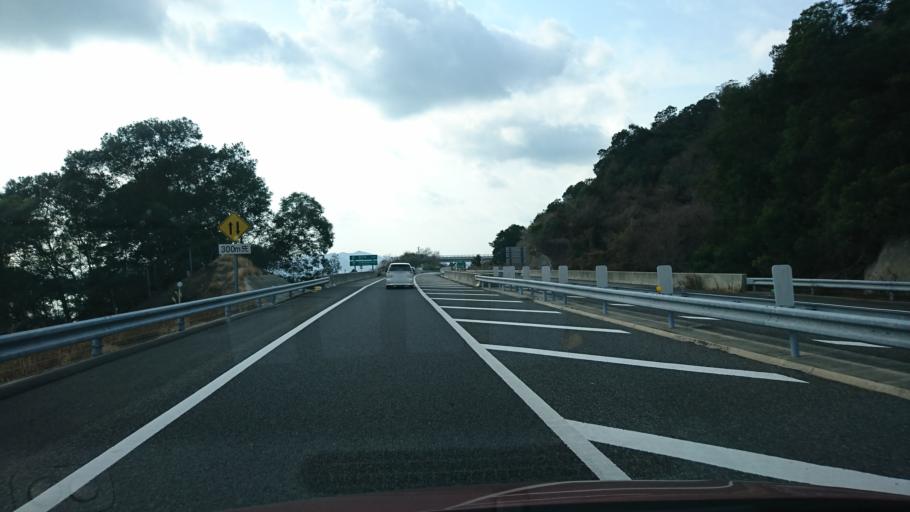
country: JP
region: Hiroshima
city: Innoshima
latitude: 34.2765
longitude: 133.1076
